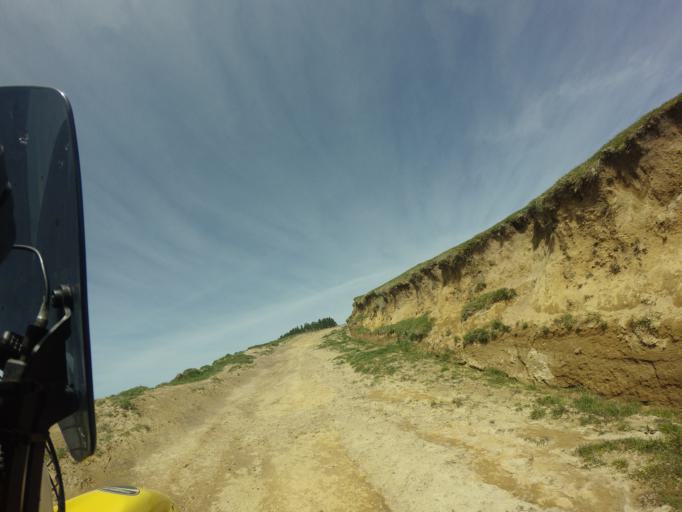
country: NZ
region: Bay of Plenty
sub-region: Opotiki District
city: Opotiki
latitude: -38.4673
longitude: 177.3784
